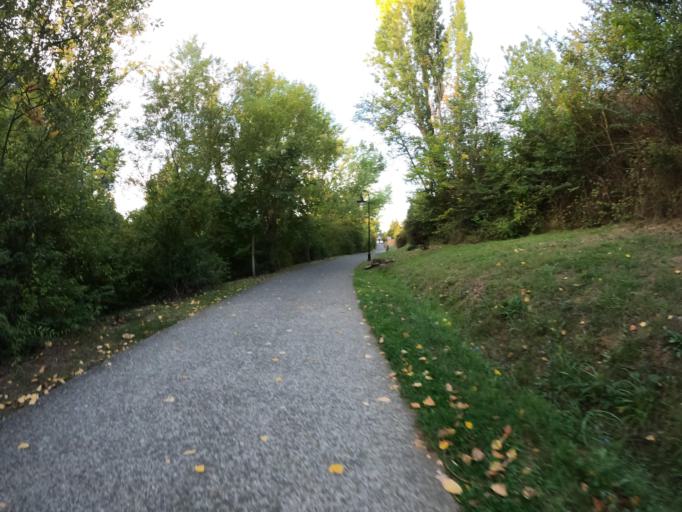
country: ES
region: Navarre
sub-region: Provincia de Navarra
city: Baranain
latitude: 42.8168
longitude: -1.6822
